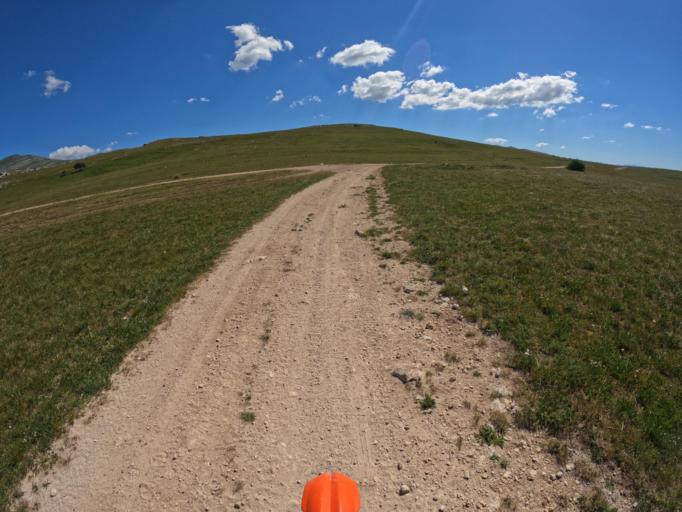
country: BA
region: Federation of Bosnia and Herzegovina
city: Livno
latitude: 43.8641
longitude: 17.0532
